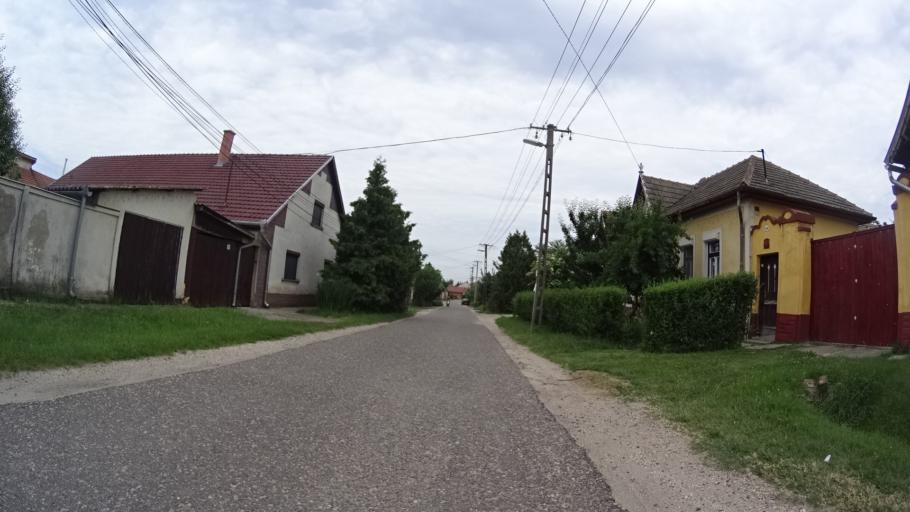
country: HU
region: Bacs-Kiskun
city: Tiszakecske
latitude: 46.9309
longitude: 20.0935
